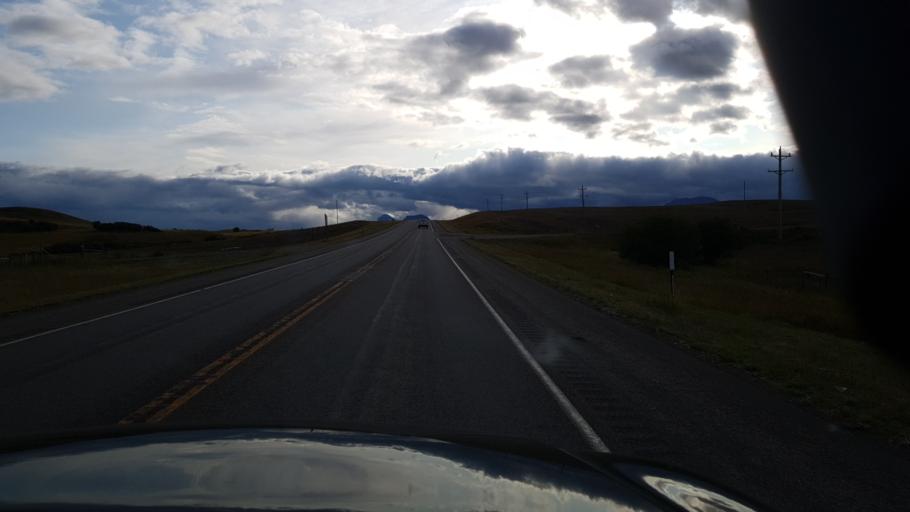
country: US
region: Montana
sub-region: Glacier County
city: South Browning
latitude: 48.5034
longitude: -113.1088
